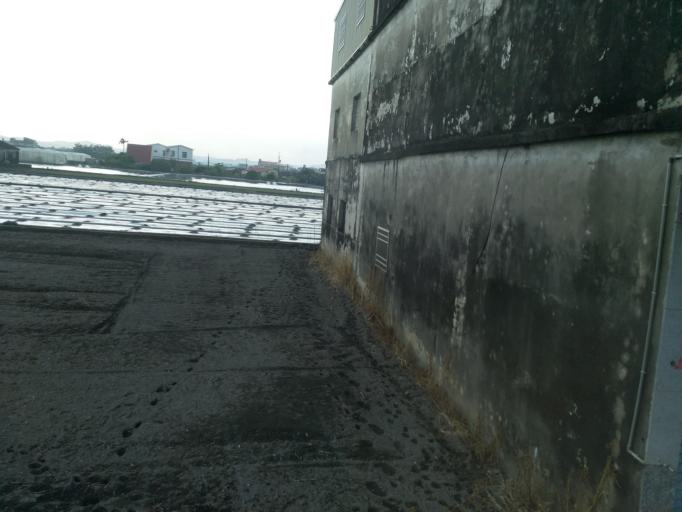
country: TW
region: Taiwan
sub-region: Pingtung
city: Pingtung
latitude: 22.8695
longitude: 120.5368
